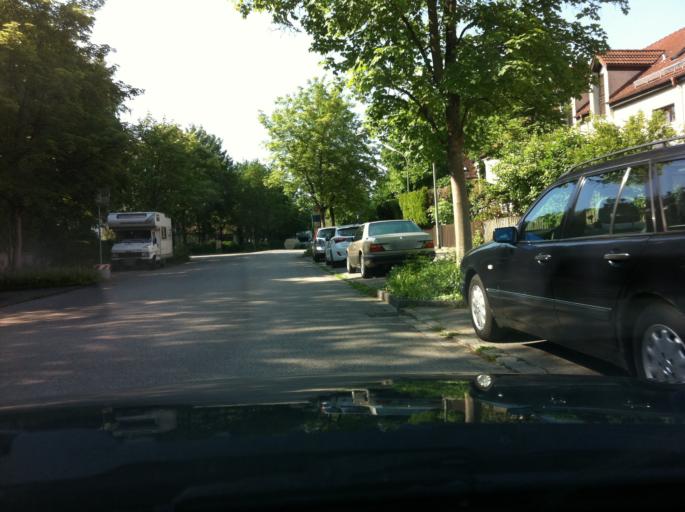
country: DE
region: Bavaria
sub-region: Upper Bavaria
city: Taufkirchen
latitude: 48.0512
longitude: 11.6154
